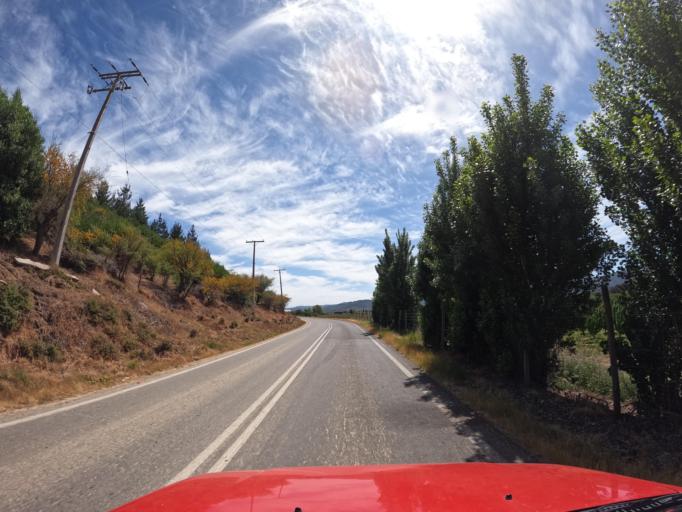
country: CL
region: Maule
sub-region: Provincia de Talca
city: Talca
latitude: -34.9890
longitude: -71.8167
